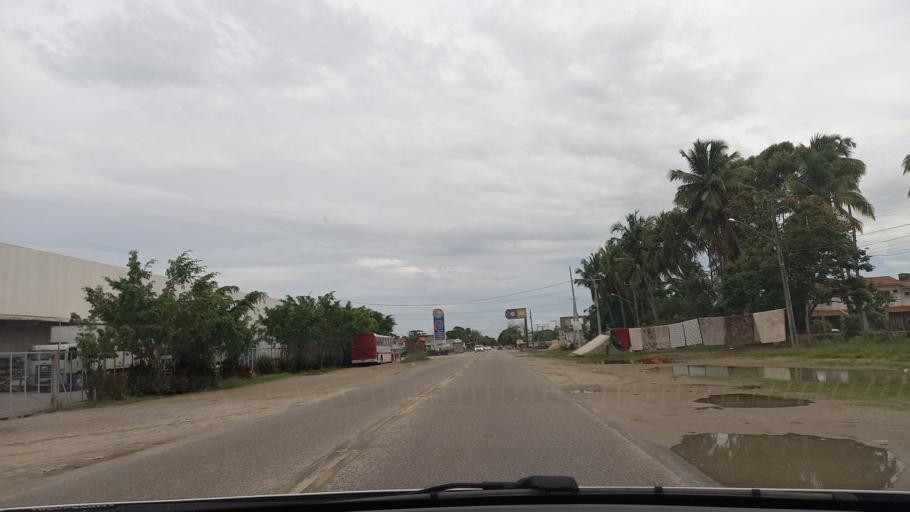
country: BR
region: Pernambuco
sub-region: Sao Jose Da Coroa Grande
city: Sao Jose da Coroa Grande
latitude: -8.8960
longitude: -35.1506
